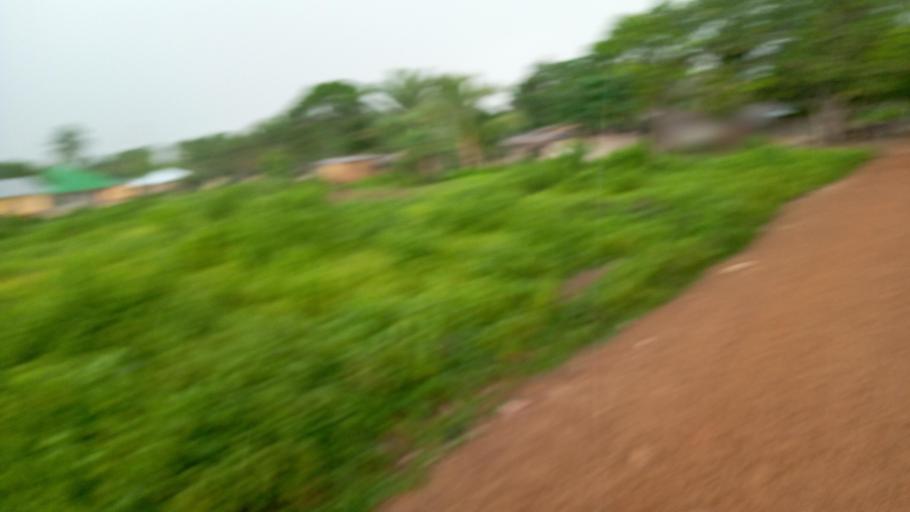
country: SL
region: Southern Province
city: Mogbwemo
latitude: 7.7830
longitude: -12.2931
